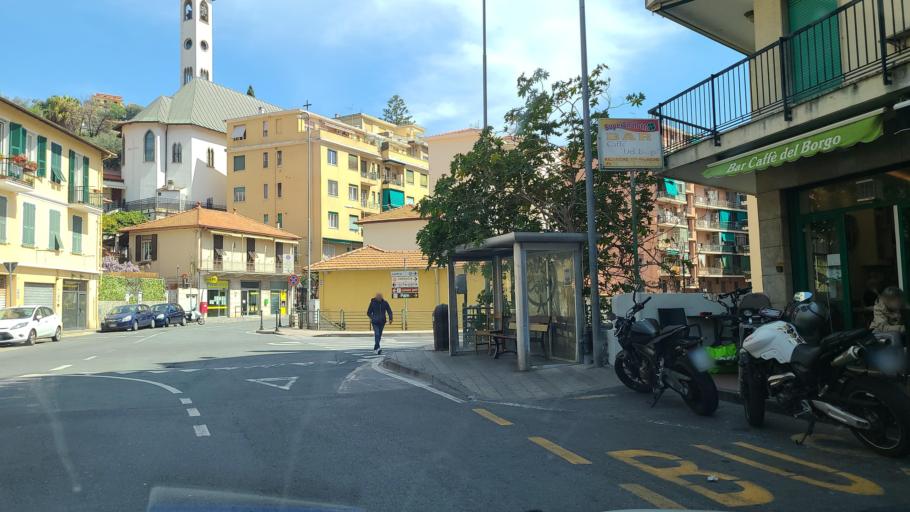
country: IT
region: Liguria
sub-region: Provincia di Imperia
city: San Remo
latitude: 43.8254
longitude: 7.7623
